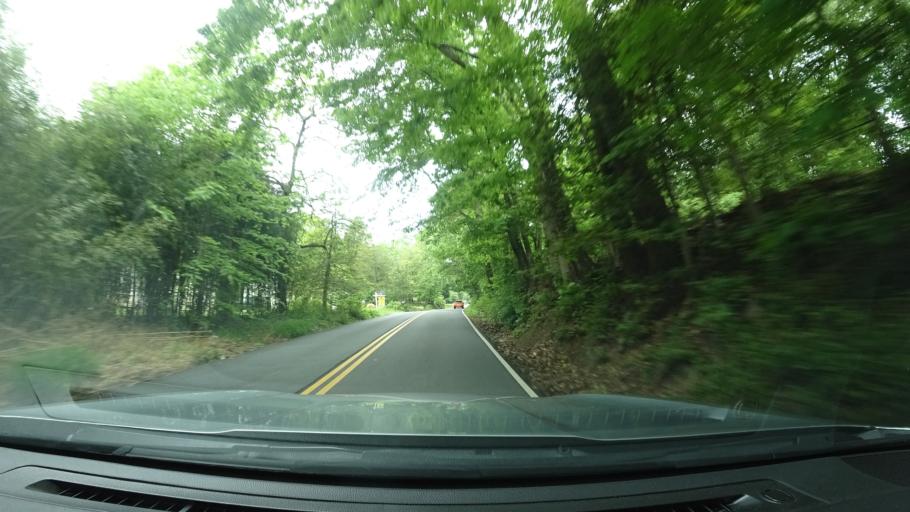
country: US
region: Virginia
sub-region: Fairfax County
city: Greenbriar
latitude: 38.8781
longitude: -77.3625
